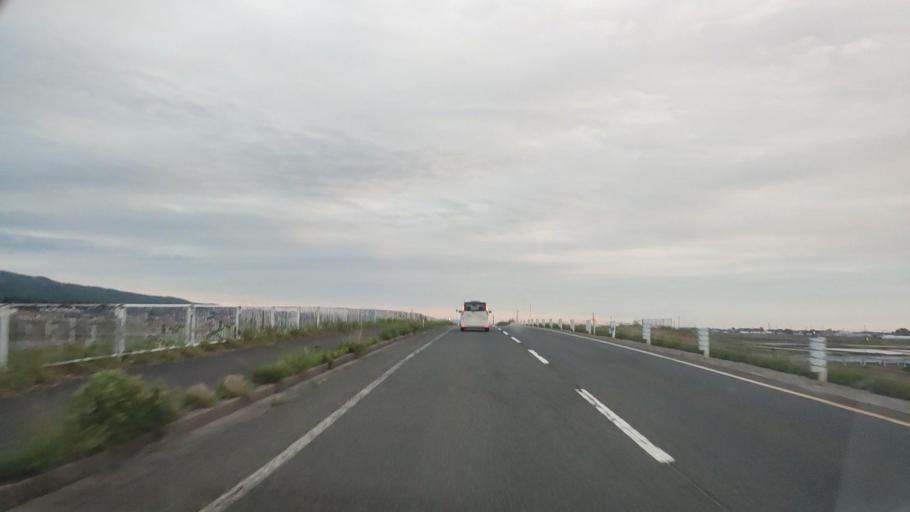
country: JP
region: Niigata
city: Niitsu-honcho
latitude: 37.7592
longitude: 139.0939
